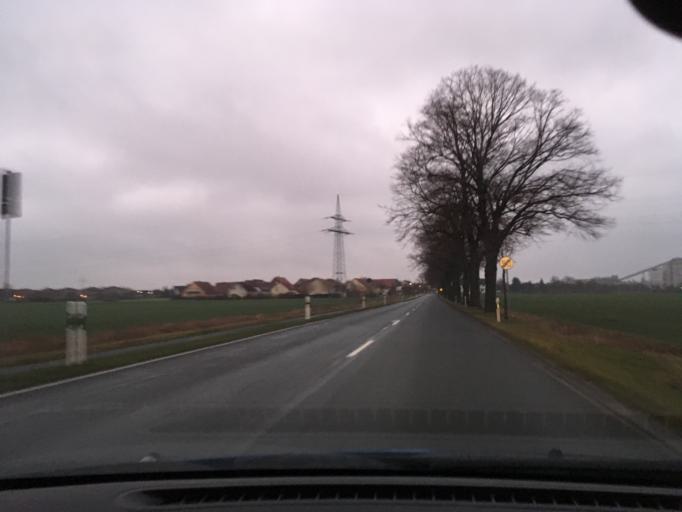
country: DE
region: Lower Saxony
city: Sehnde
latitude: 52.3539
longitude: 9.9030
